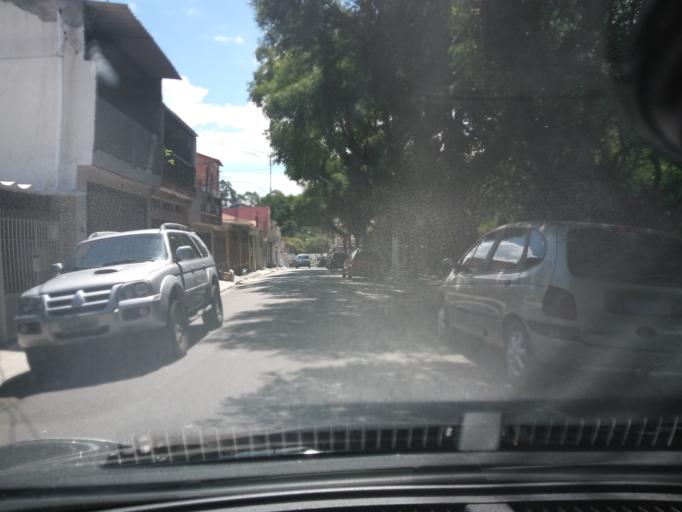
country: BR
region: Sao Paulo
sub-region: Sao Bernardo Do Campo
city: Sao Bernardo do Campo
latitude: -23.7030
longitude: -46.5747
